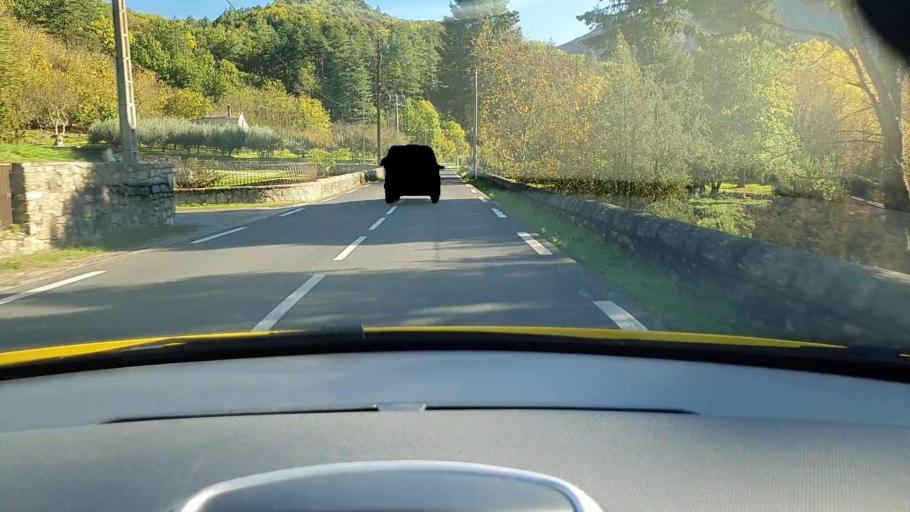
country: FR
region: Languedoc-Roussillon
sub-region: Departement du Gard
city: Le Vigan
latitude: 43.9749
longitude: 3.5093
